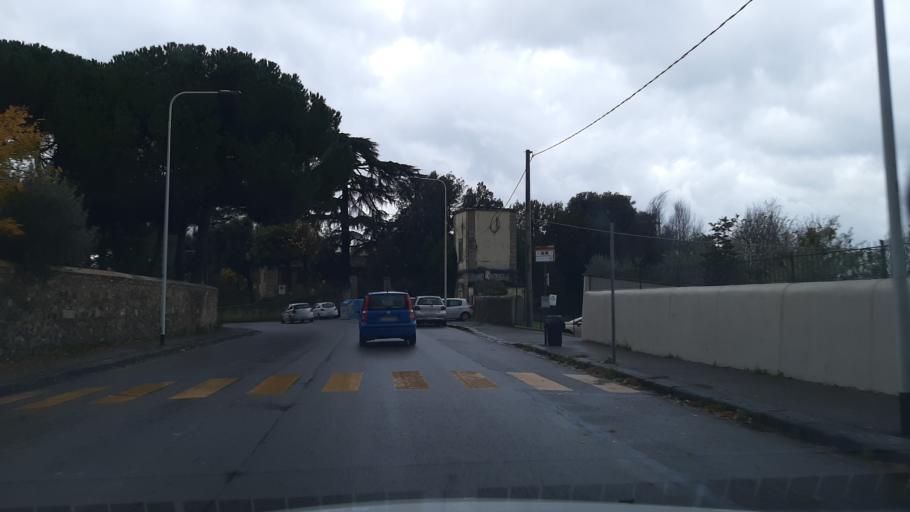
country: IT
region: Tuscany
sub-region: Province of Florence
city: Florence
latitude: 43.8109
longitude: 11.2499
